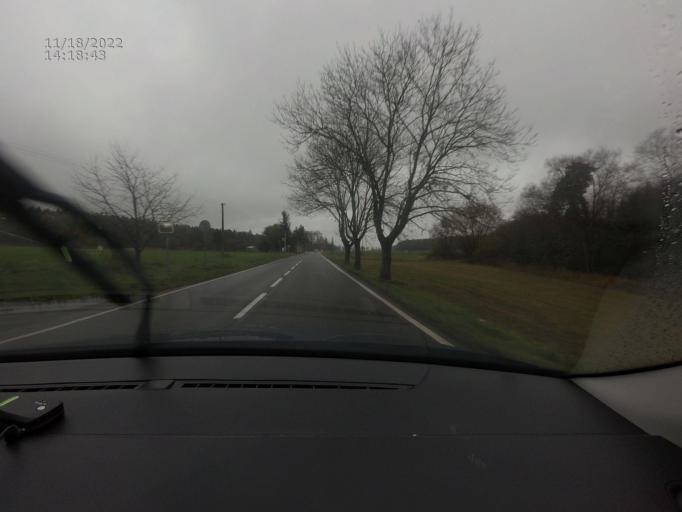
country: CZ
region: Jihocesky
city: Mirotice
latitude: 49.4394
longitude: 14.0570
